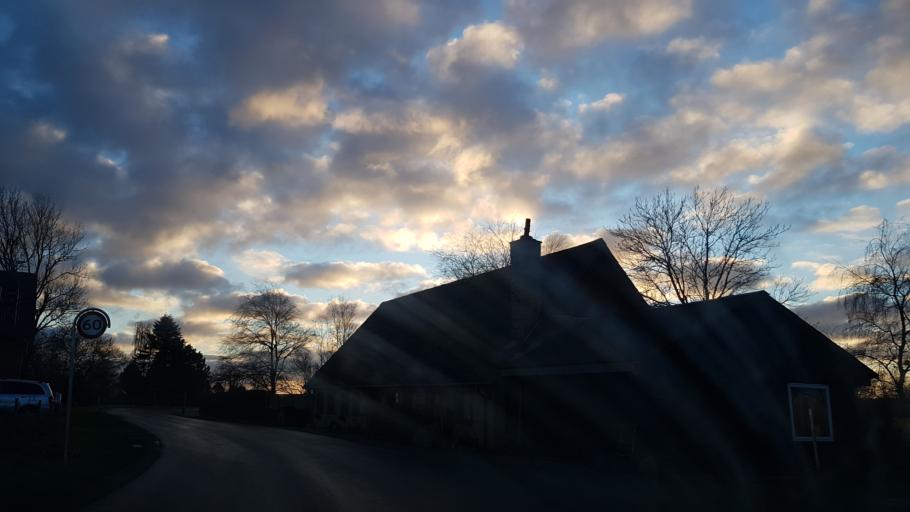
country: DK
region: South Denmark
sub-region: Kolding Kommune
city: Vamdrup
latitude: 55.3651
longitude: 9.3419
